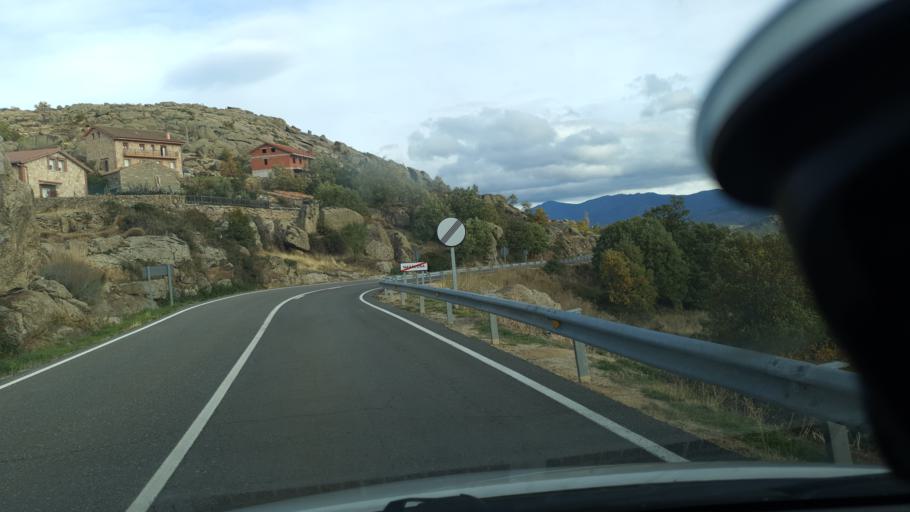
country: ES
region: Castille and Leon
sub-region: Provincia de Avila
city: Navalosa
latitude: 40.3977
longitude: -4.9303
